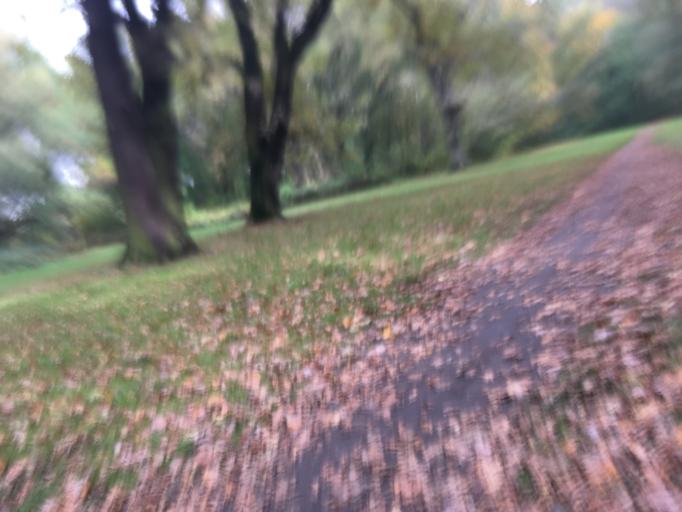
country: DE
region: Berlin
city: Plaenterwald
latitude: 52.4840
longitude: 13.4754
